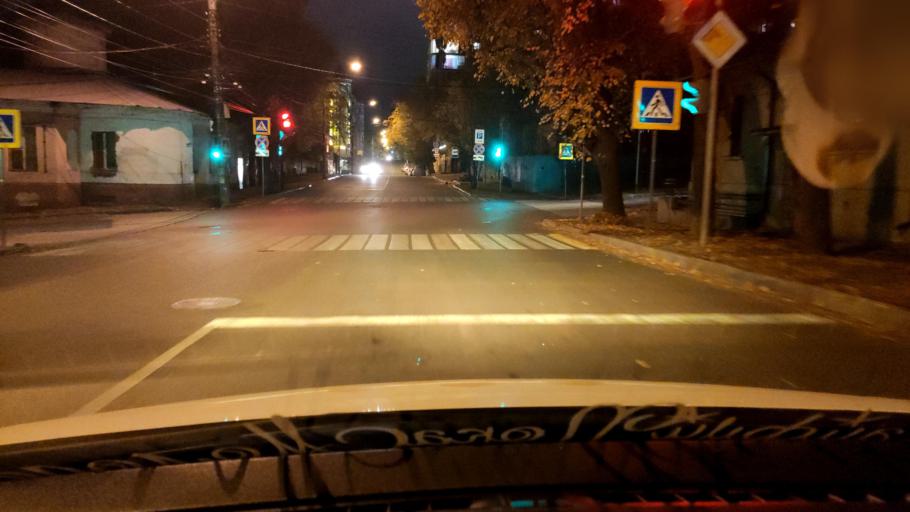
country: RU
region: Voronezj
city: Voronezh
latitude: 51.6791
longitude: 39.2192
